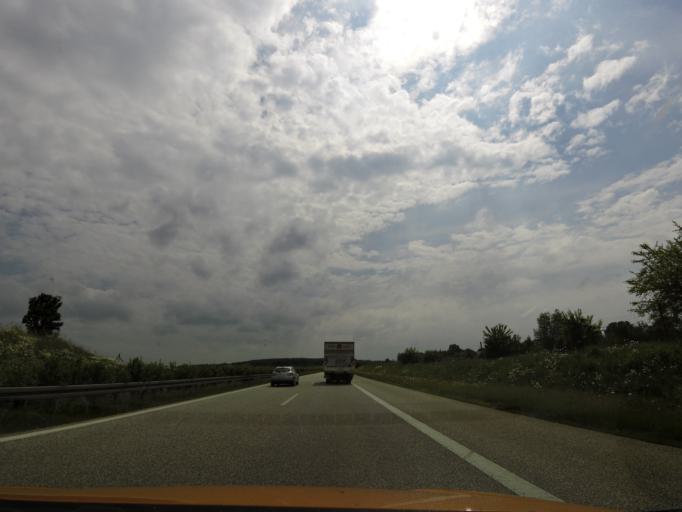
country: DE
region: Mecklenburg-Vorpommern
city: Leezen
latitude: 53.6681
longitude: 11.5140
